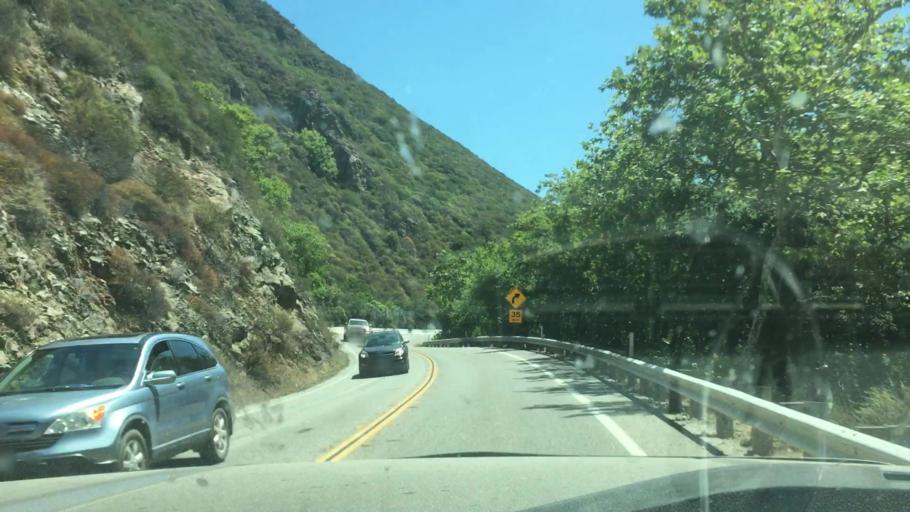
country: US
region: California
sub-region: San Luis Obispo County
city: Atascadero
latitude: 35.4284
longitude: -120.7587
